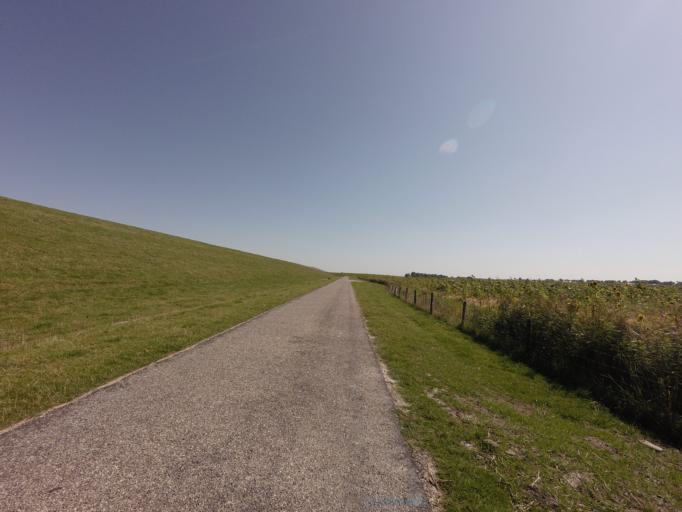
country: NL
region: Friesland
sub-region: Gemeente Dongeradeel
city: Anjum
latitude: 53.4011
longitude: 6.0941
